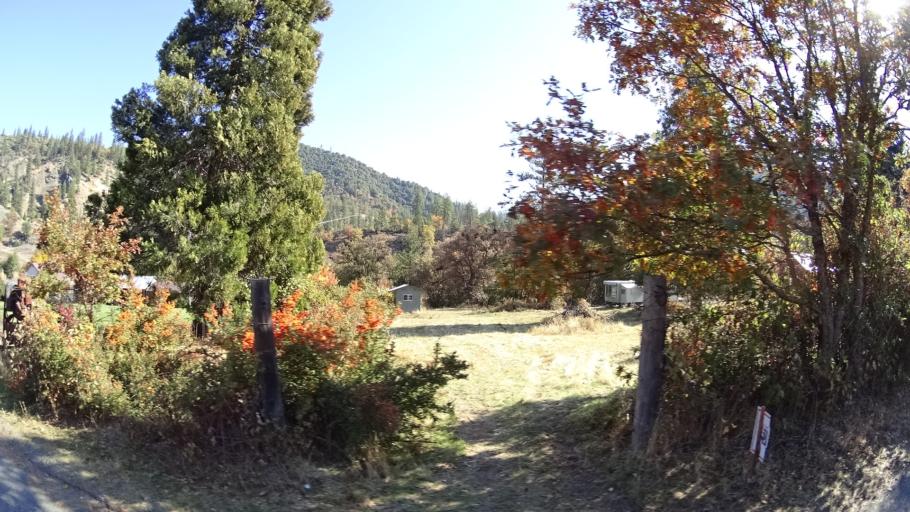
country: US
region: California
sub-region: Siskiyou County
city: Yreka
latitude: 41.7416
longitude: -123.0043
